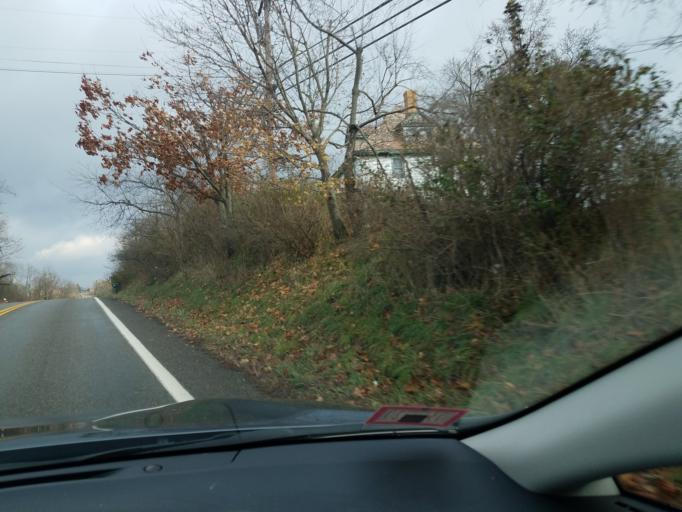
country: US
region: Pennsylvania
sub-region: Allegheny County
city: Franklin Park
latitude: 40.6035
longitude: -80.0993
